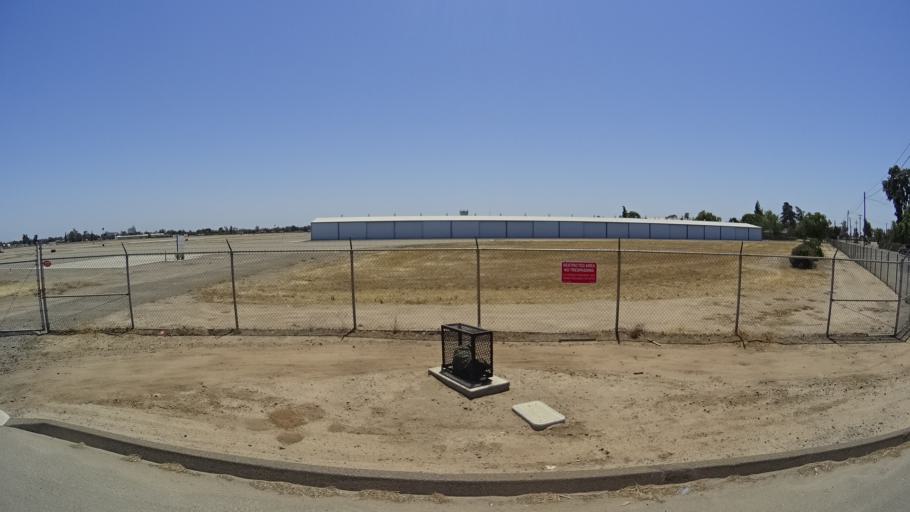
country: US
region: California
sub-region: Fresno County
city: West Park
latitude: 36.7344
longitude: -119.8265
